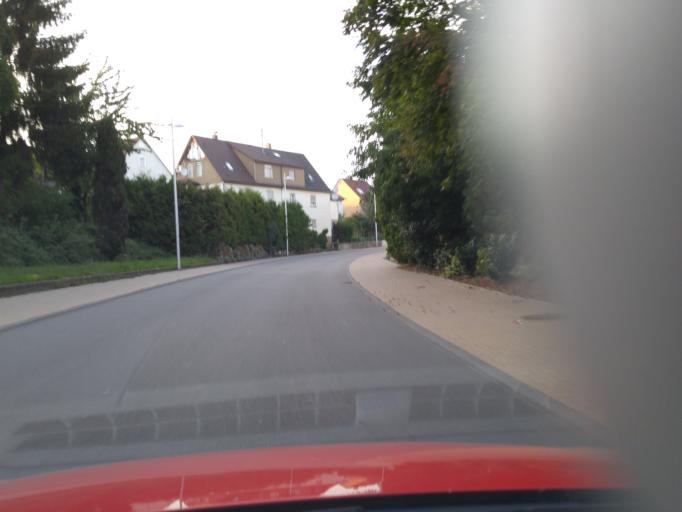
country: DE
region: Baden-Wuerttemberg
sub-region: Regierungsbezirk Stuttgart
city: Untereisesheim
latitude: 49.1948
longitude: 9.2021
